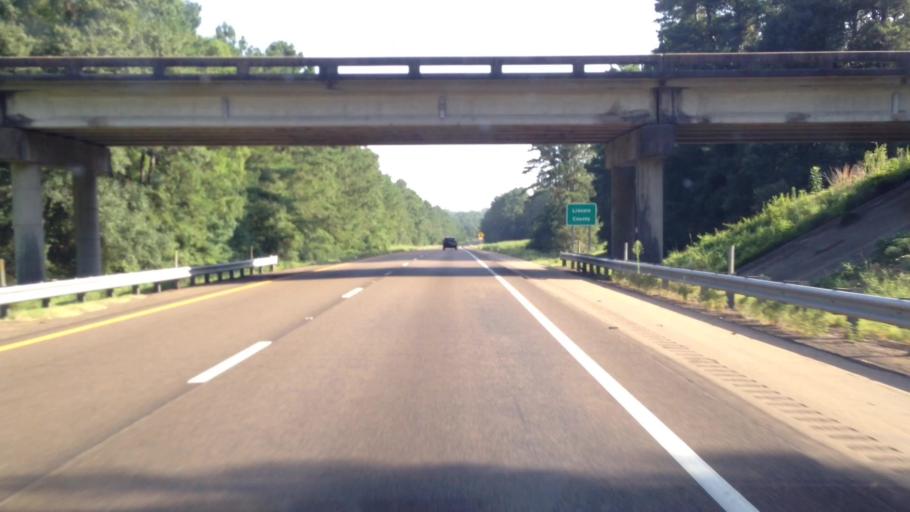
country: US
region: Mississippi
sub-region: Pike County
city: Summit
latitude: 31.3489
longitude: -90.4786
